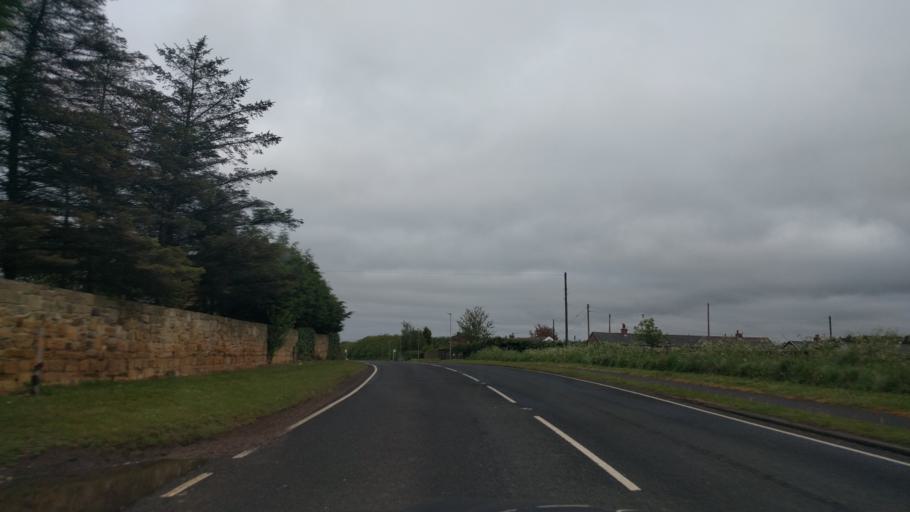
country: GB
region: England
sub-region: Northumberland
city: Pegswood
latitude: 55.1614
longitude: -1.6269
